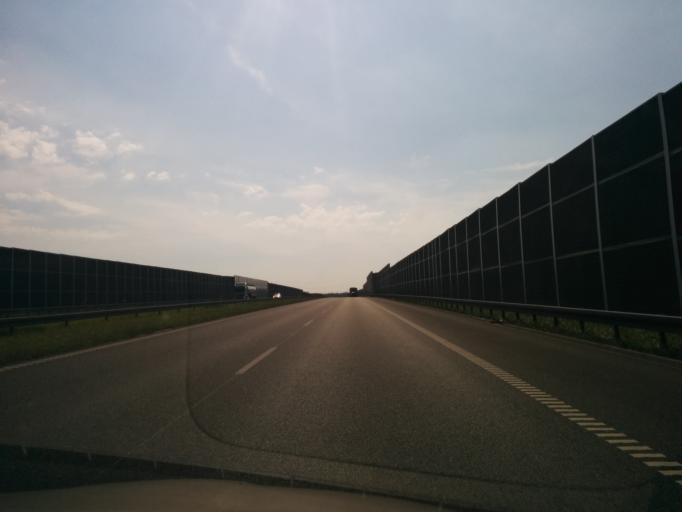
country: PL
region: Silesian Voivodeship
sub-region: Powiat tarnogorski
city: Wieszowa
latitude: 50.3858
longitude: 18.8128
